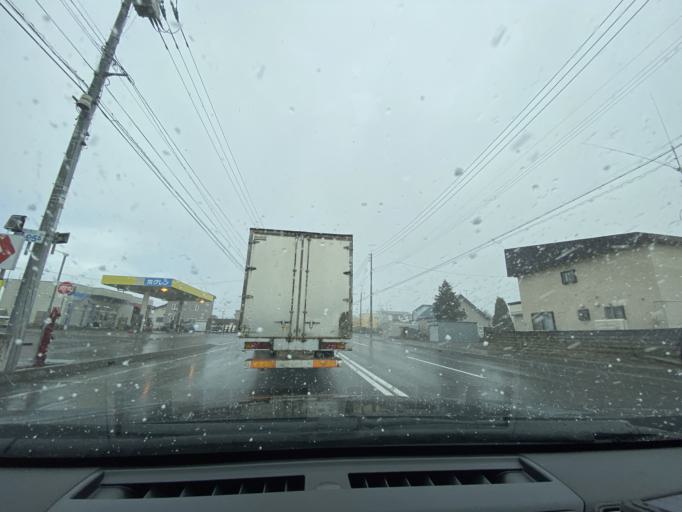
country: JP
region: Hokkaido
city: Takikawa
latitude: 43.6282
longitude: 141.9425
